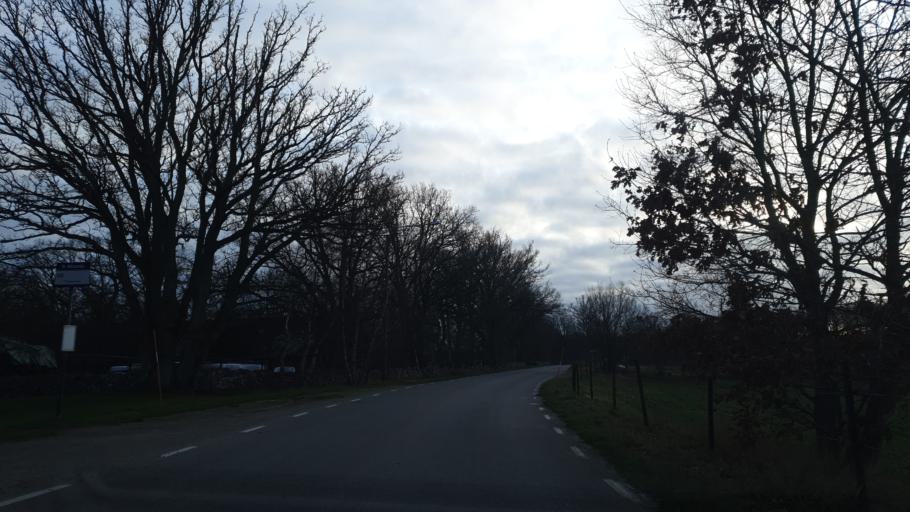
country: SE
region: Blekinge
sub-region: Karlskrona Kommun
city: Jaemjoe
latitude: 56.1786
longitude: 15.9362
